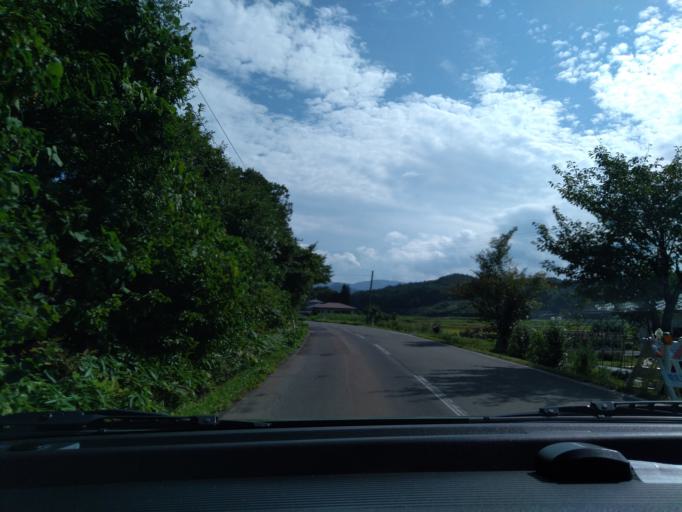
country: JP
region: Iwate
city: Shizukuishi
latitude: 39.6567
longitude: 140.9923
